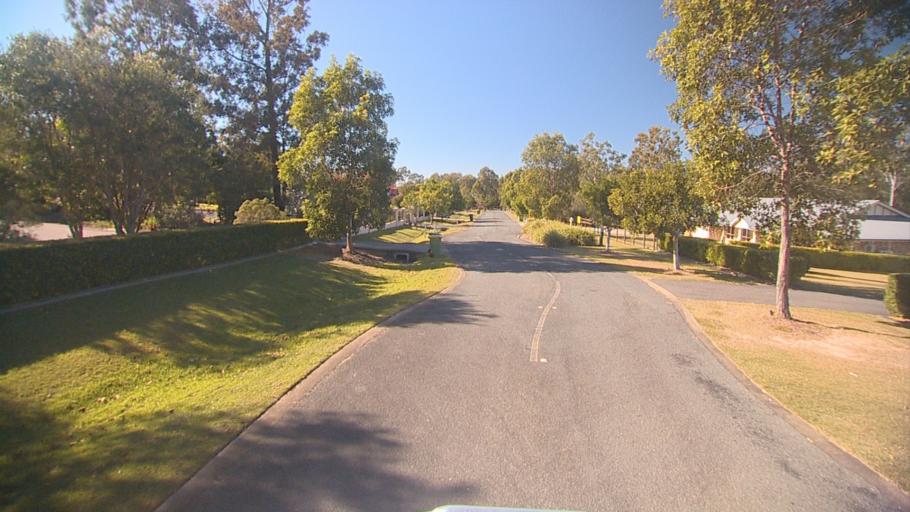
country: AU
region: Queensland
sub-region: Logan
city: North Maclean
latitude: -27.7495
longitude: 152.9613
